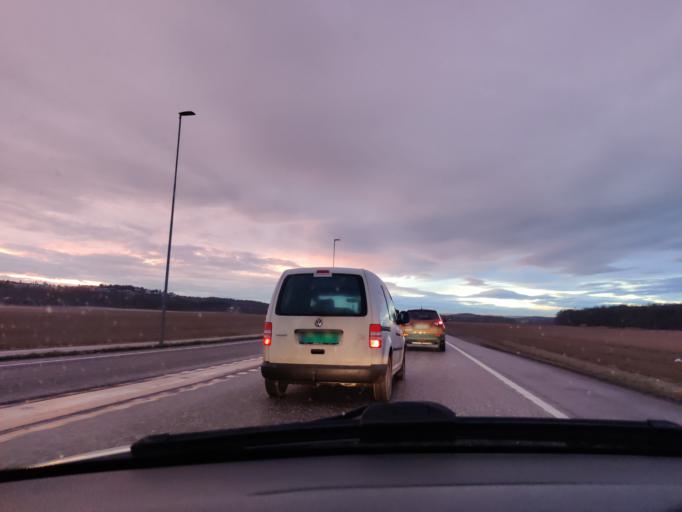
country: NO
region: Vestfold
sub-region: Tonsberg
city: Tonsberg
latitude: 59.2820
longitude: 10.3893
